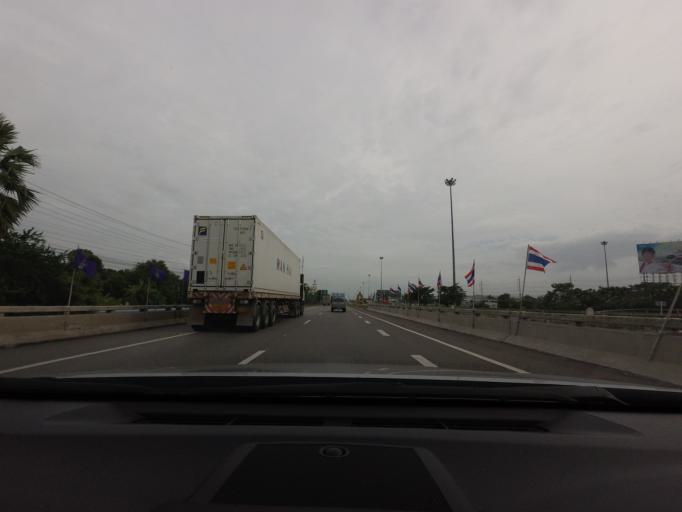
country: TH
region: Ratchaburi
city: Pak Tho
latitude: 13.3381
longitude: 99.8311
